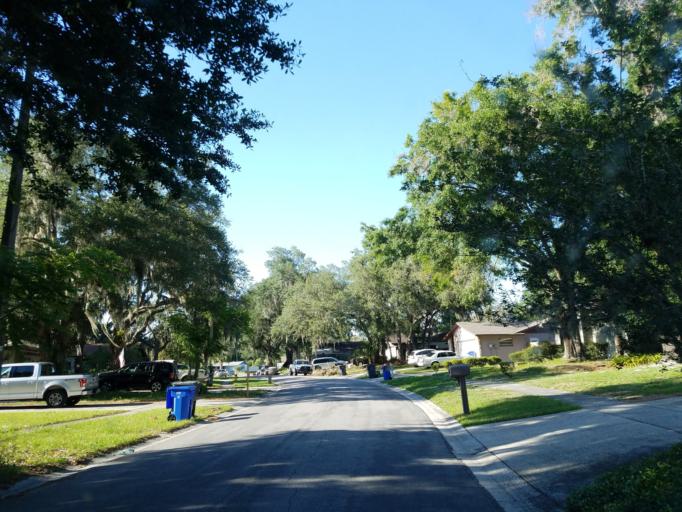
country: US
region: Florida
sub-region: Hillsborough County
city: Riverview
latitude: 27.8877
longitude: -82.2975
